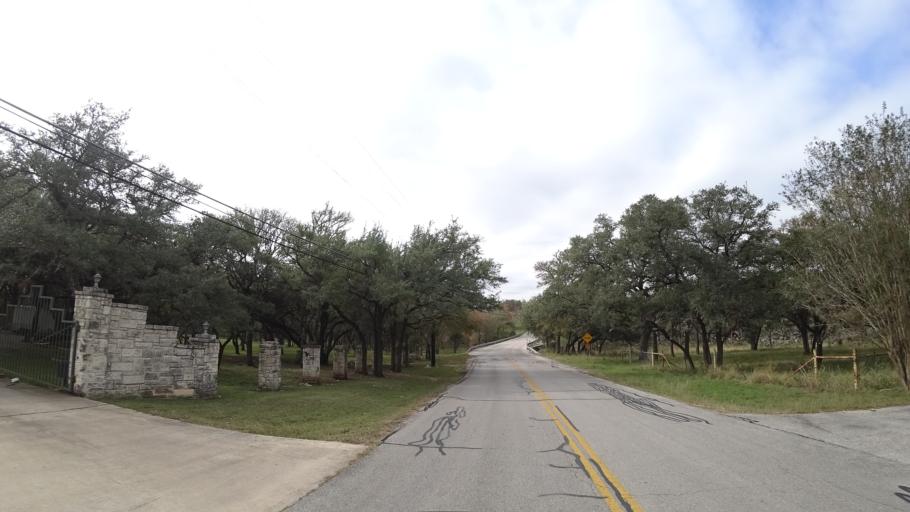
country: US
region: Texas
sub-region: Travis County
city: Shady Hollow
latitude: 30.1384
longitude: -97.8764
